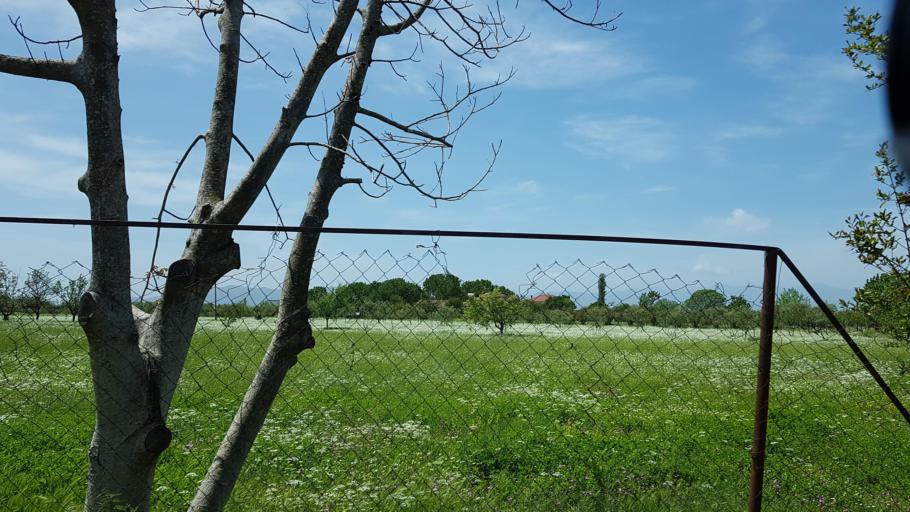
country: AL
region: Shkoder
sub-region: Rrethi i Malesia e Madhe
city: Gruemire
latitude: 42.1370
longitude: 19.5470
